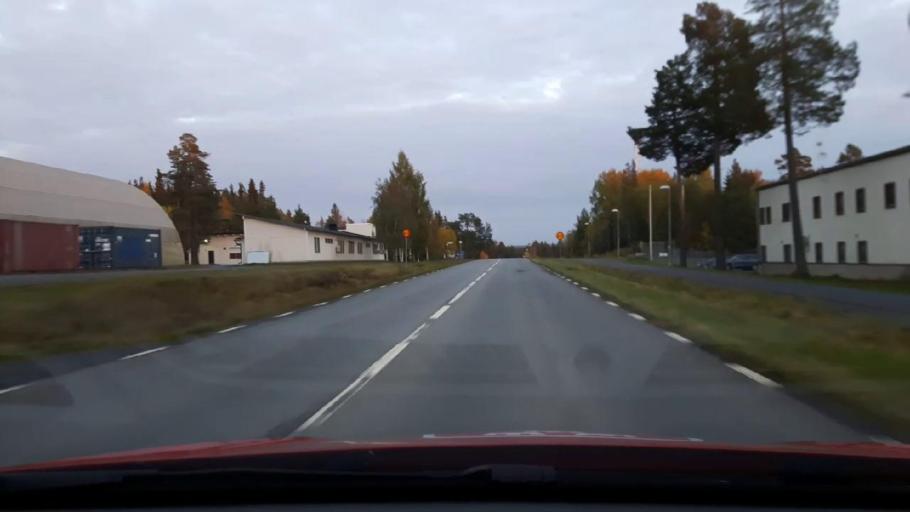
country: SE
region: Jaemtland
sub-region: OEstersunds Kommun
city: Ostersund
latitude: 63.2170
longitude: 14.6134
